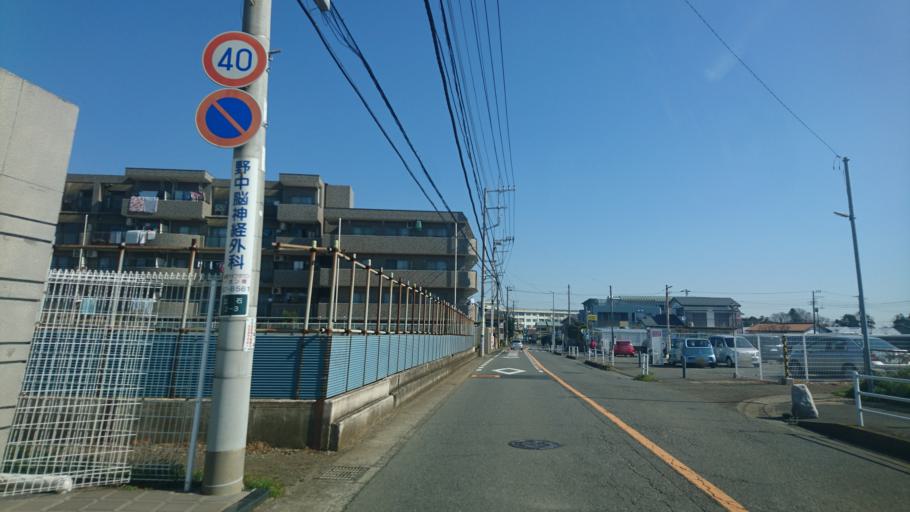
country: JP
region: Kanagawa
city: Fujisawa
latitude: 35.3647
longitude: 139.4809
